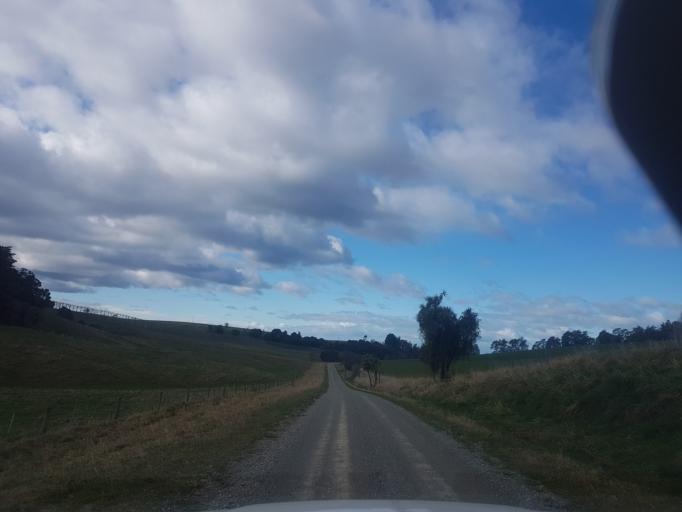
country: NZ
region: Canterbury
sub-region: Timaru District
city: Pleasant Point
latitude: -44.1839
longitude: 171.1363
